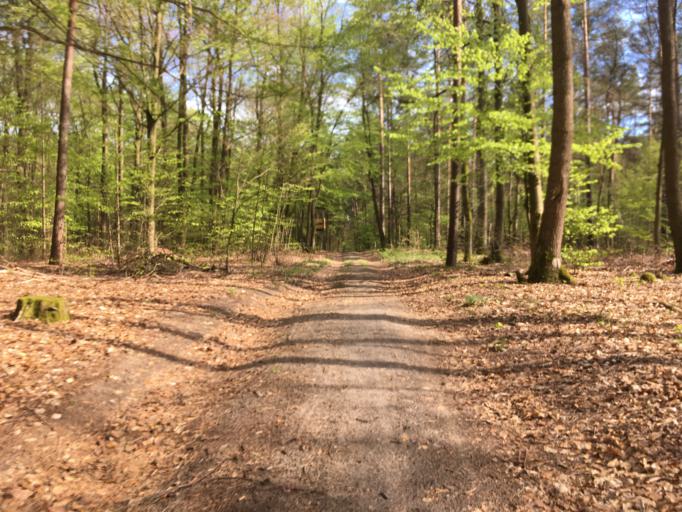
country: DE
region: Brandenburg
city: Bernau bei Berlin
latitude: 52.7230
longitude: 13.5597
